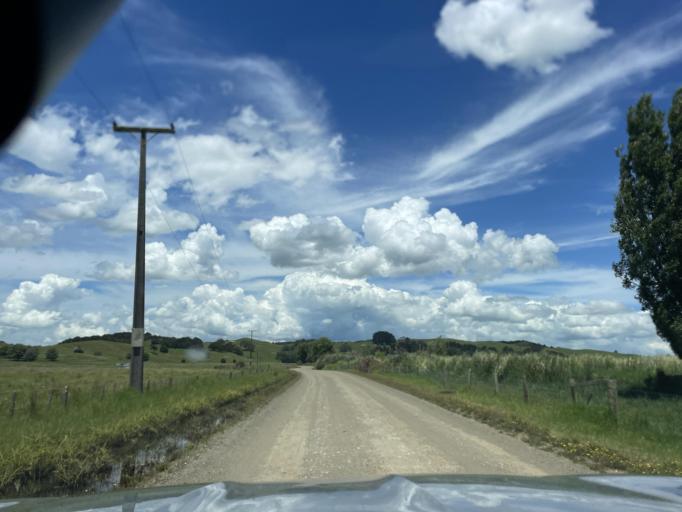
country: NZ
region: Northland
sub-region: Kaipara District
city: Dargaville
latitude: -35.8973
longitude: 173.9159
